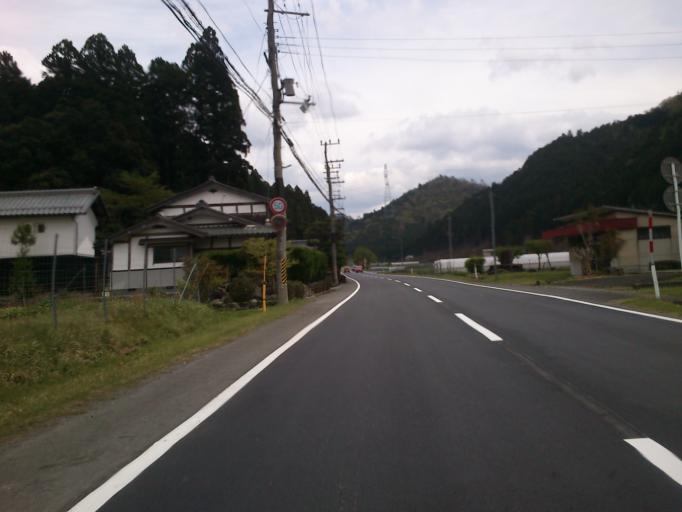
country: JP
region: Kyoto
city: Kameoka
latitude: 35.2061
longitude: 135.6065
